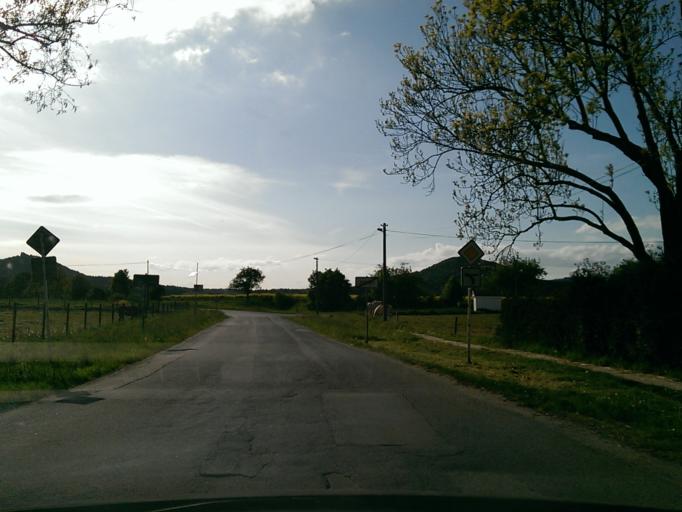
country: CZ
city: Doksy
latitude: 50.5559
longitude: 14.6164
